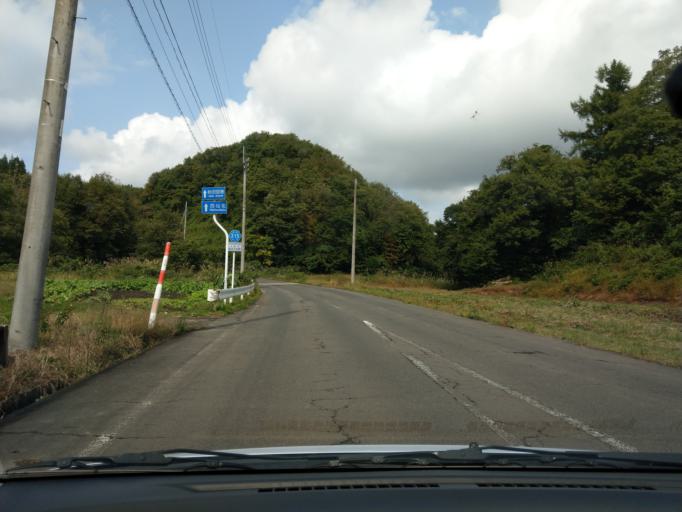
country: JP
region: Akita
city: Omagari
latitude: 39.4413
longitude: 140.3341
